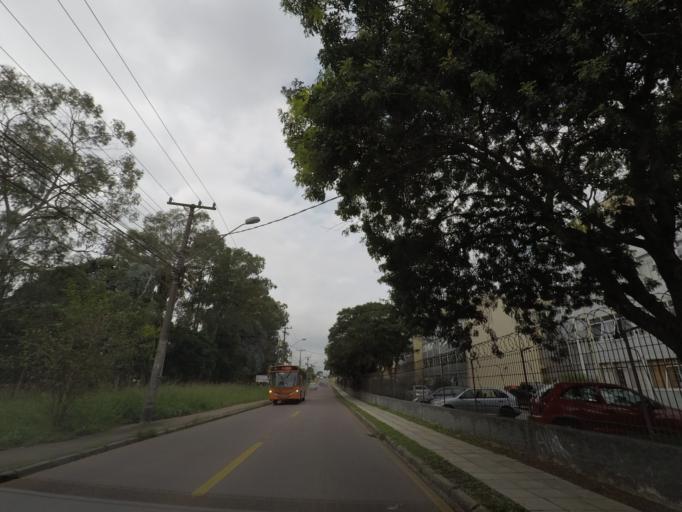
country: BR
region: Parana
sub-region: Curitiba
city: Curitiba
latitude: -25.4942
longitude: -49.3128
